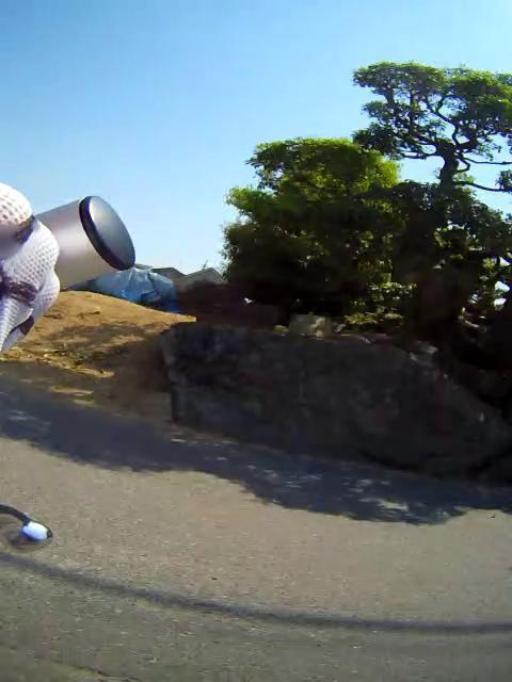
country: JP
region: Osaka
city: Matsubara
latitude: 34.5849
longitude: 135.5507
